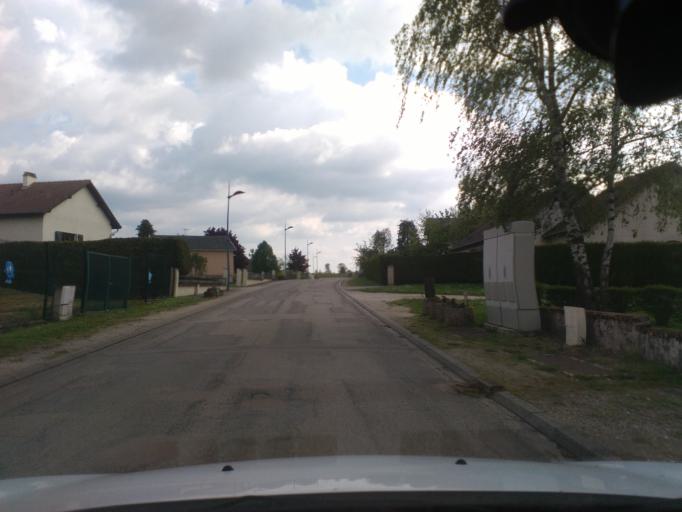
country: FR
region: Lorraine
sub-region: Departement des Vosges
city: Mirecourt
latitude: 48.3195
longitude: 6.1474
